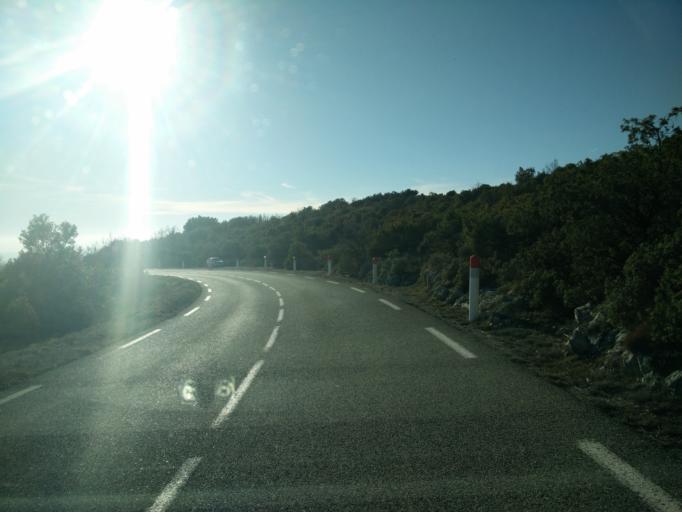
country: FR
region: Provence-Alpes-Cote d'Azur
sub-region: Departement des Alpes-Maritimes
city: Saint-Vallier-de-Thiey
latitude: 43.7060
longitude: 6.8191
